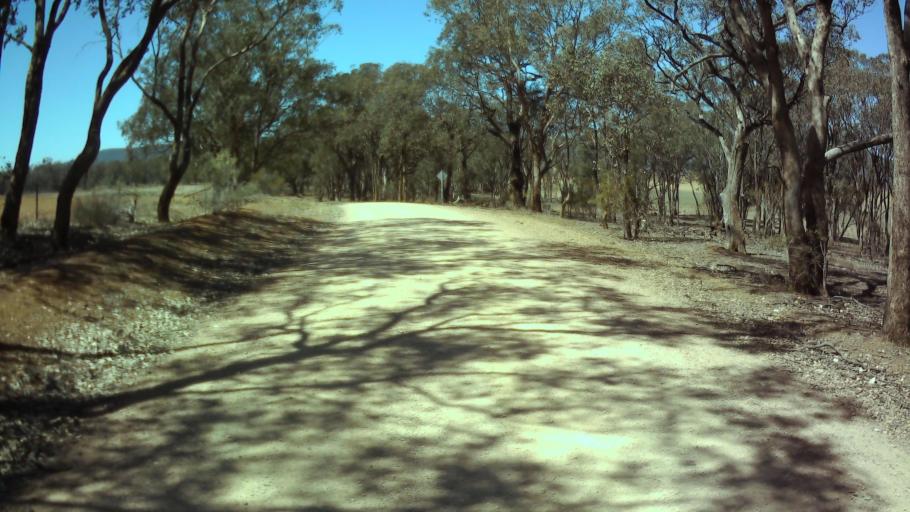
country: AU
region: New South Wales
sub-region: Weddin
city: Grenfell
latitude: -33.9325
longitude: 148.0772
